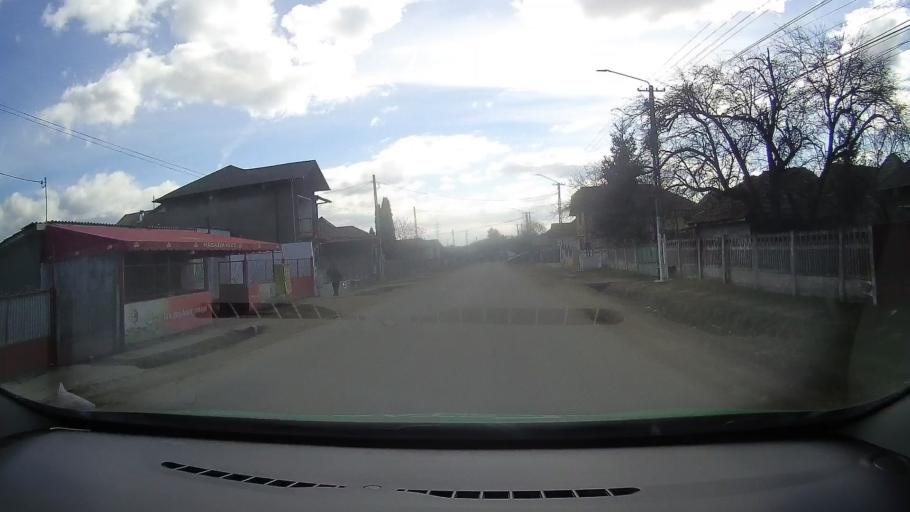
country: RO
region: Dambovita
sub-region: Comuna Doicesti
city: Doicesti
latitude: 44.9779
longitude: 25.3915
